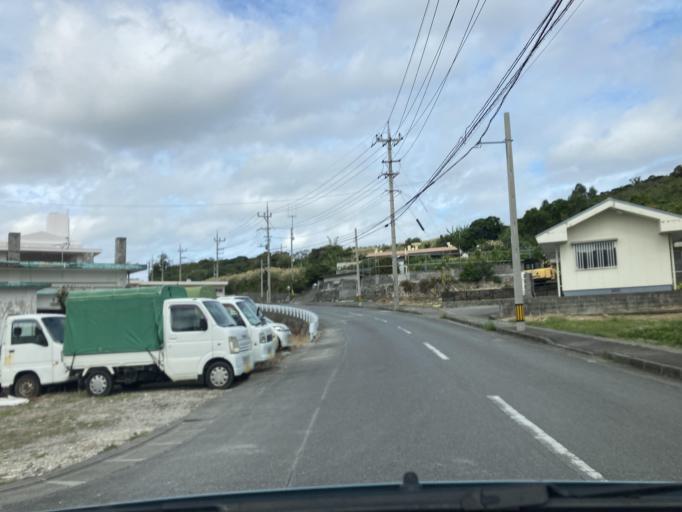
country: JP
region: Okinawa
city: Ginowan
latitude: 26.2066
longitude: 127.7468
